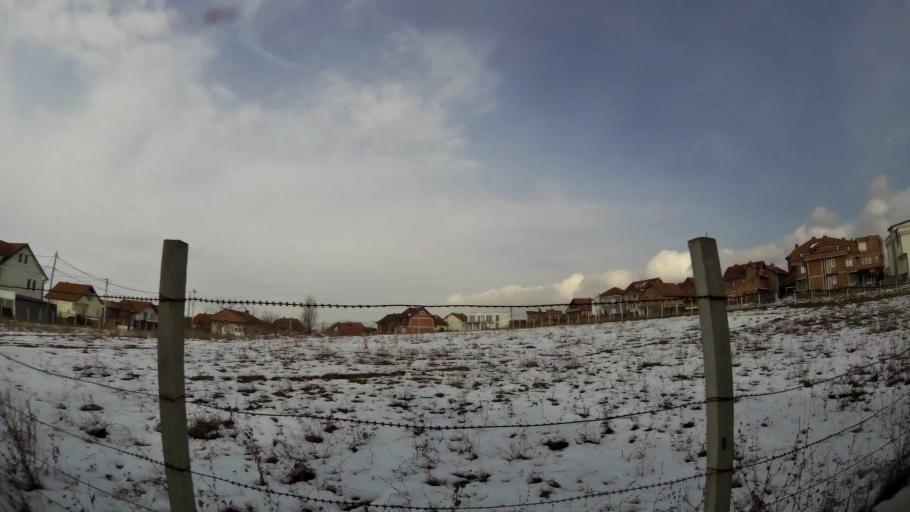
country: XK
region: Pristina
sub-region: Komuna e Prishtines
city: Pristina
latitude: 42.6886
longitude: 21.1553
